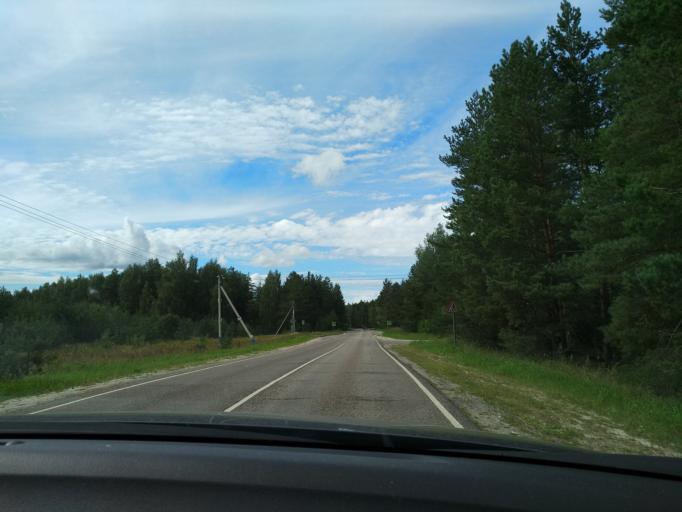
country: RU
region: Moskovskaya
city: Krasnyy Tkach
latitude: 55.3972
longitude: 39.1347
